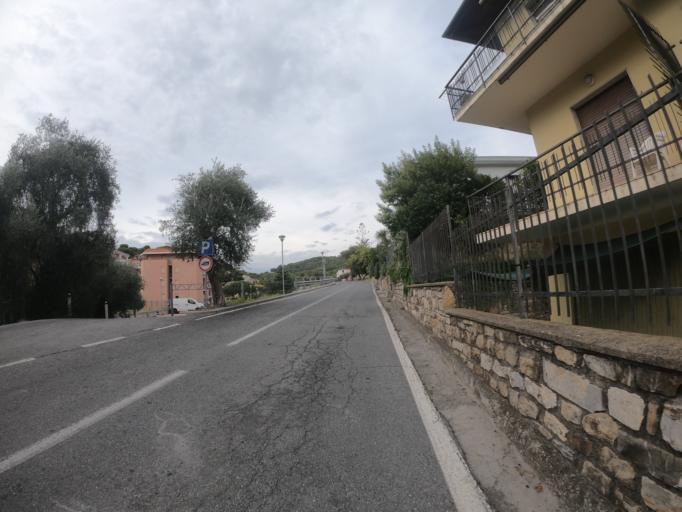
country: IT
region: Liguria
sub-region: Provincia di Savona
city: Marina di Andora
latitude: 43.9542
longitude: 8.1517
